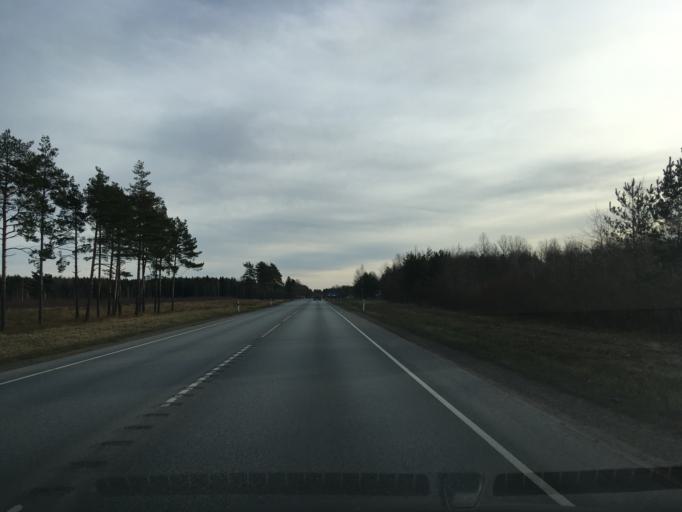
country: EE
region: Ida-Virumaa
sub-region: Johvi vald
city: Johvi
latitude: 59.3670
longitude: 27.4278
